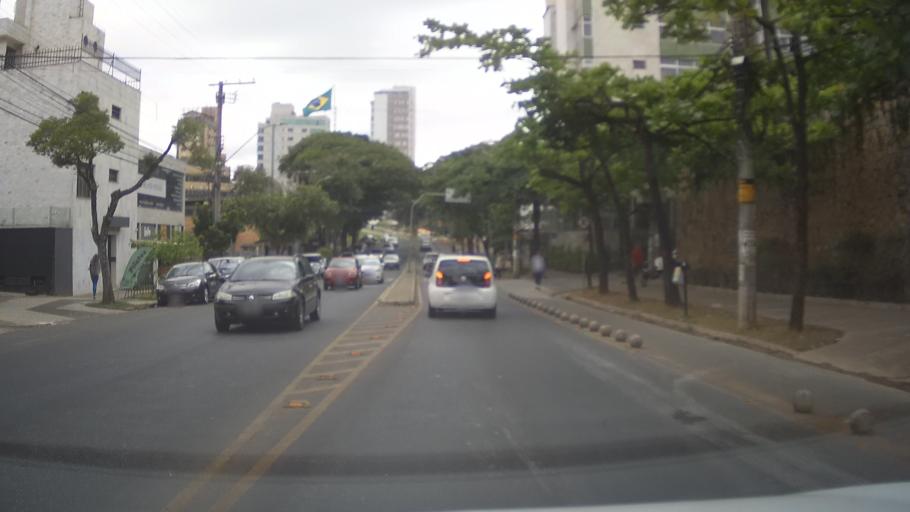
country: BR
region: Minas Gerais
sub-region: Belo Horizonte
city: Belo Horizonte
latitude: -19.9499
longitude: -43.9217
